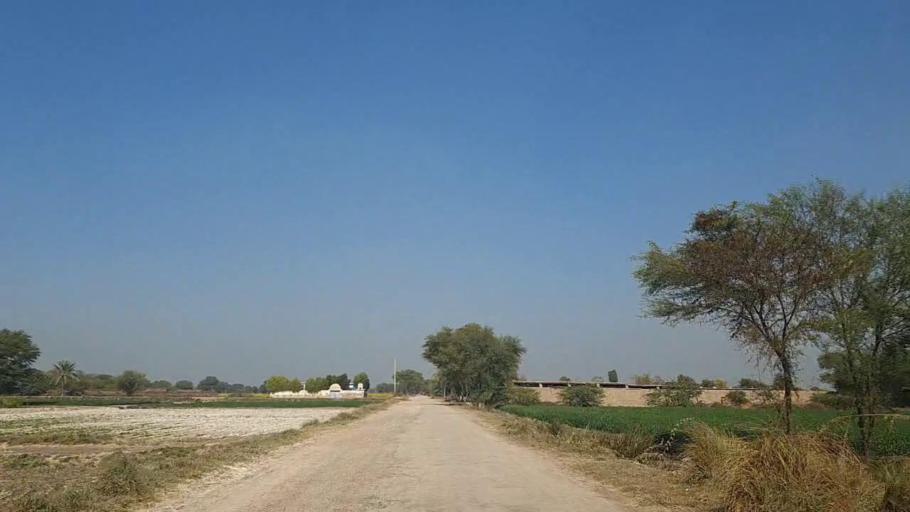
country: PK
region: Sindh
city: Nawabshah
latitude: 26.2272
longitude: 68.3380
